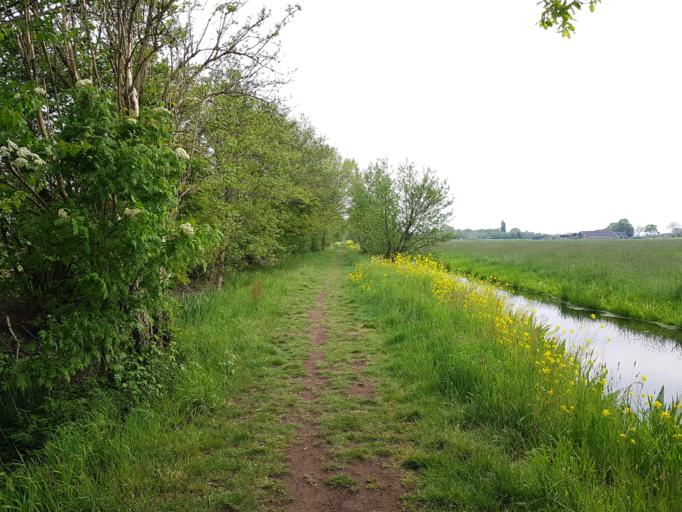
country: NL
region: South Holland
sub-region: Gemeente Vlist
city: Haastrecht
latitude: 51.9908
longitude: 4.7542
